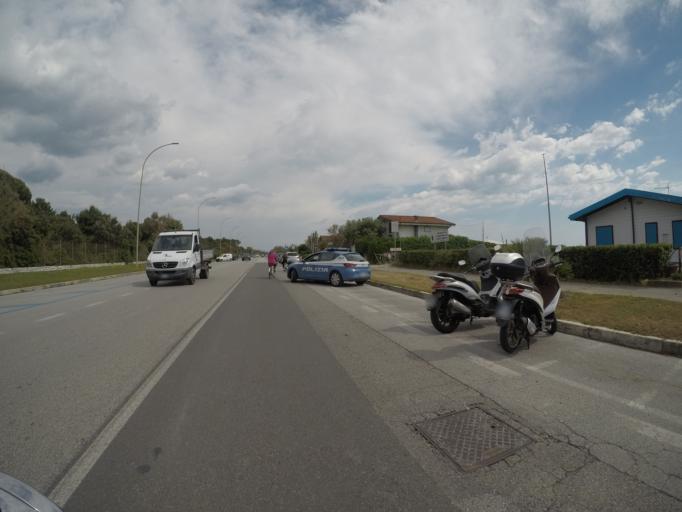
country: IT
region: Tuscany
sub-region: Provincia di Massa-Carrara
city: Massa
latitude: 44.0001
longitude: 10.1115
